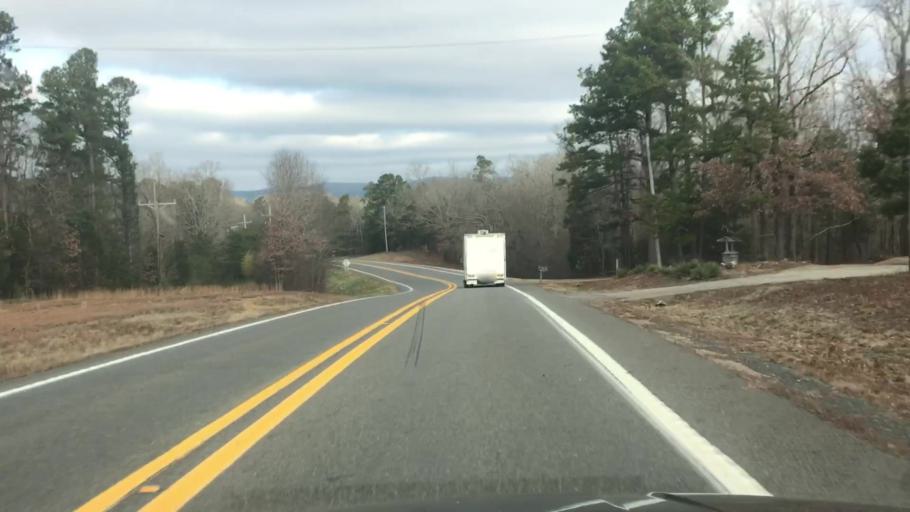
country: US
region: Arkansas
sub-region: Montgomery County
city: Mount Ida
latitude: 34.6203
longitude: -93.7227
